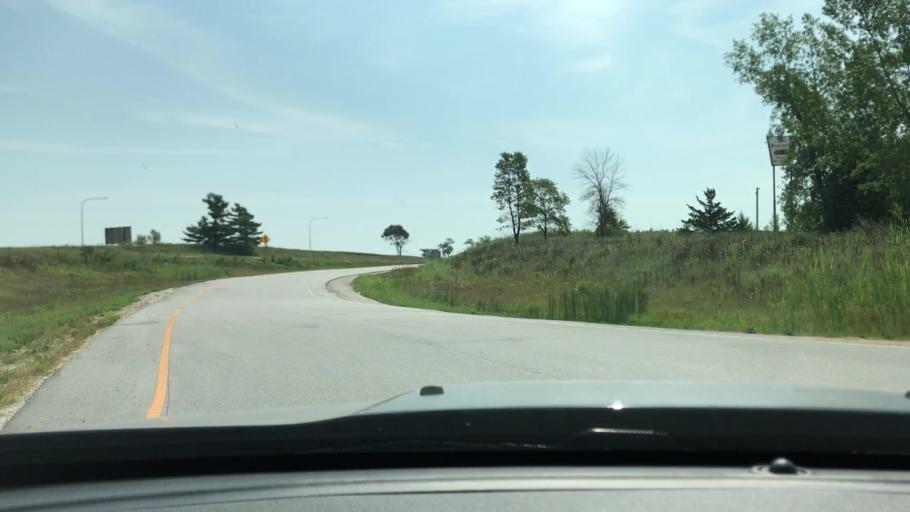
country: US
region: Illinois
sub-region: Henry County
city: Geneseo
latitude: 41.4292
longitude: -90.1574
